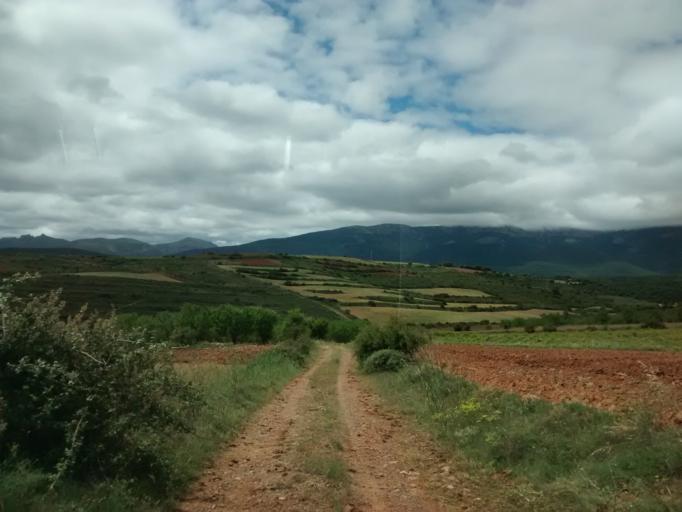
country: ES
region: Aragon
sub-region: Provincia de Zaragoza
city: Trasmoz
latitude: 41.8351
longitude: -1.7402
